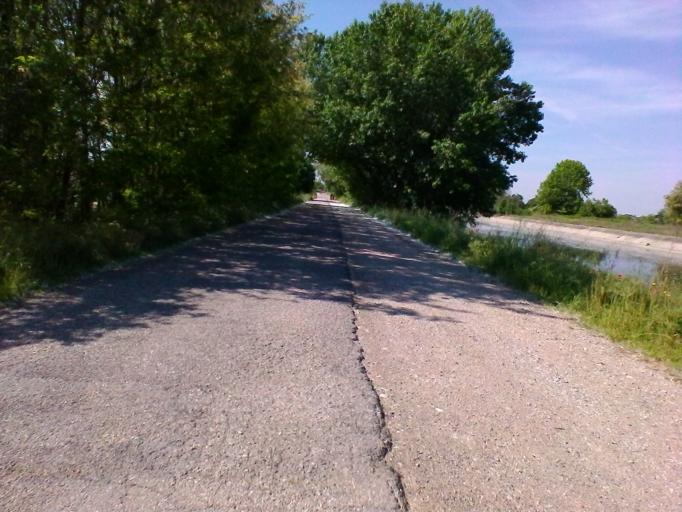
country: IT
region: Lombardy
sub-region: Provincia di Mantova
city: Soave
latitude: 45.2231
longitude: 10.7224
